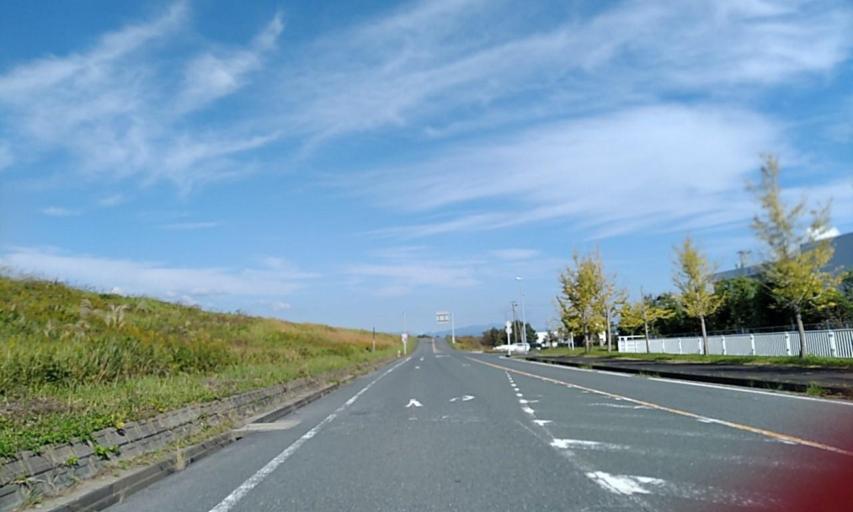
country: JP
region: Shizuoka
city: Hamakita
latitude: 34.7640
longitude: 137.8238
